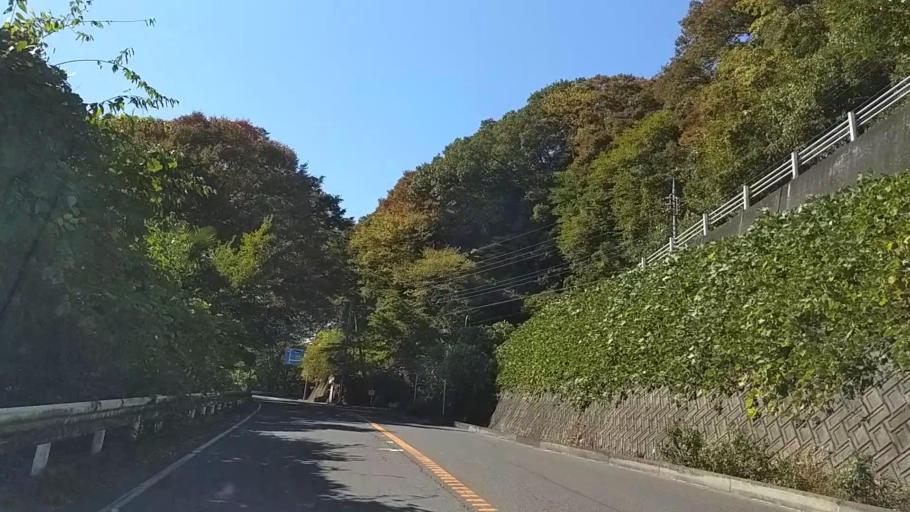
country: JP
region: Yamanashi
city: Uenohara
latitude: 35.6202
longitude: 139.1177
